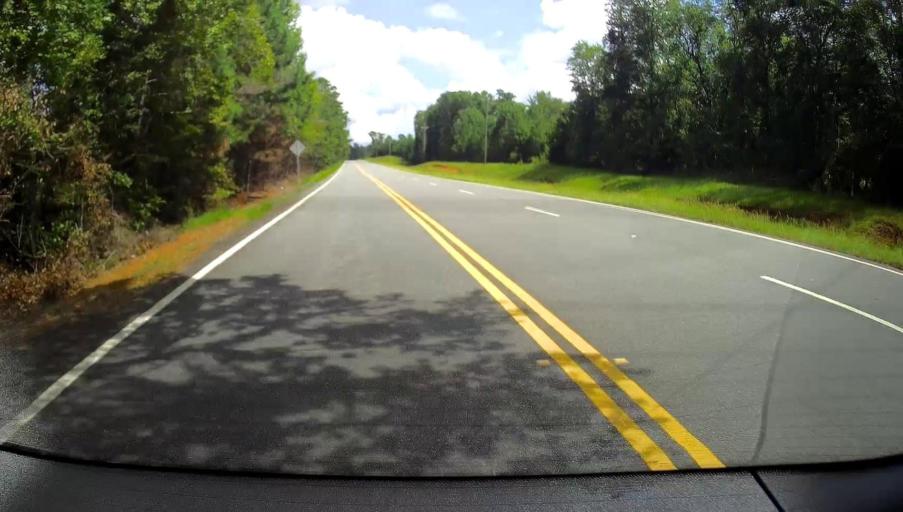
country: US
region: Georgia
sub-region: Bibb County
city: West Point
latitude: 32.8688
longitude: -83.9091
